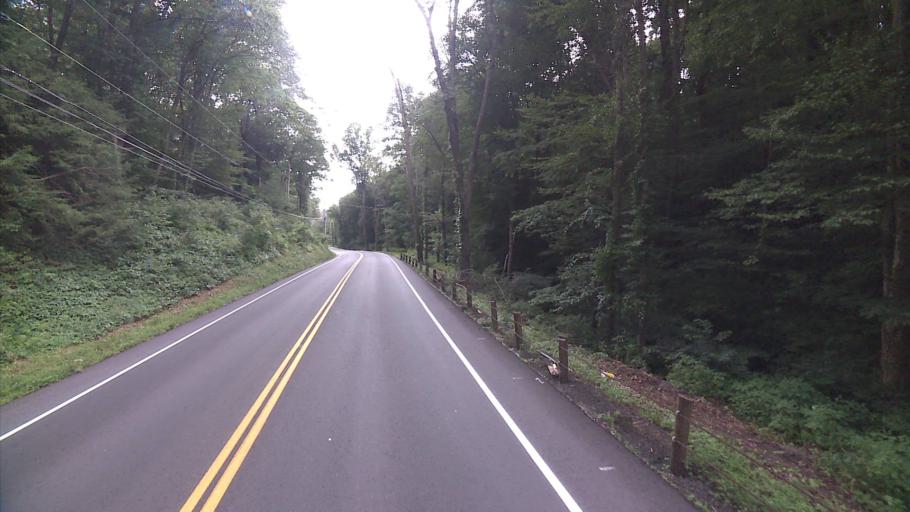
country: US
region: Connecticut
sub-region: New Haven County
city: Heritage Village
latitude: 41.5213
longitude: -73.2650
